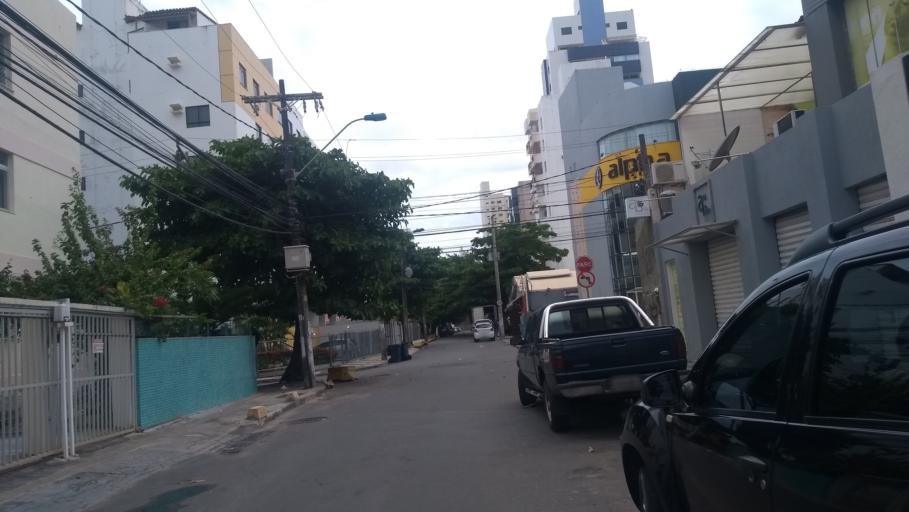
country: BR
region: Bahia
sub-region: Salvador
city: Salvador
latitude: -12.9940
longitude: -38.4468
